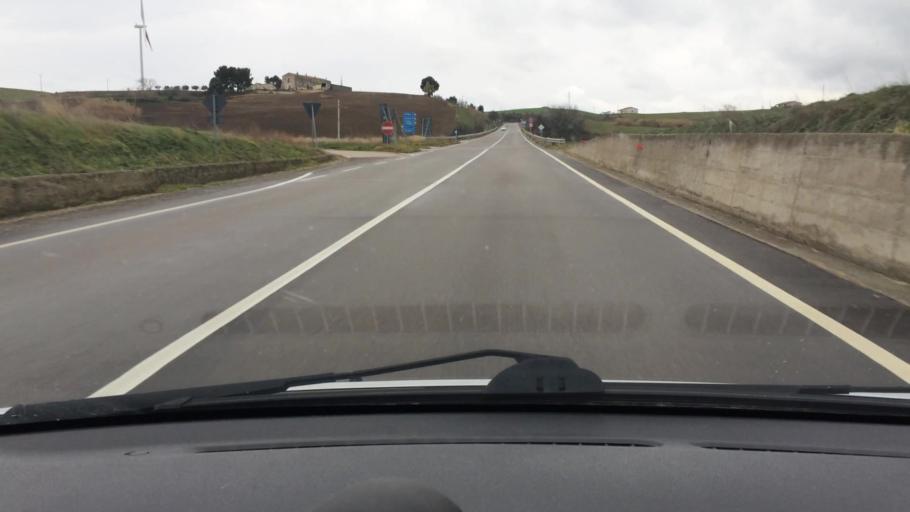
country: IT
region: Basilicate
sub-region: Provincia di Potenza
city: San Chirico Nuovo
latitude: 40.7667
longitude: 16.1036
